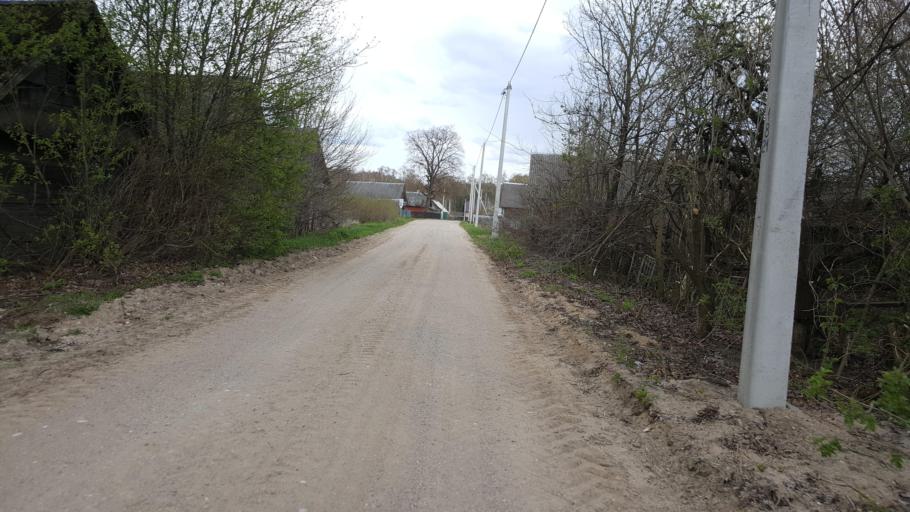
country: BY
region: Brest
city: Kamyanyets
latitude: 52.4005
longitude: 23.7311
